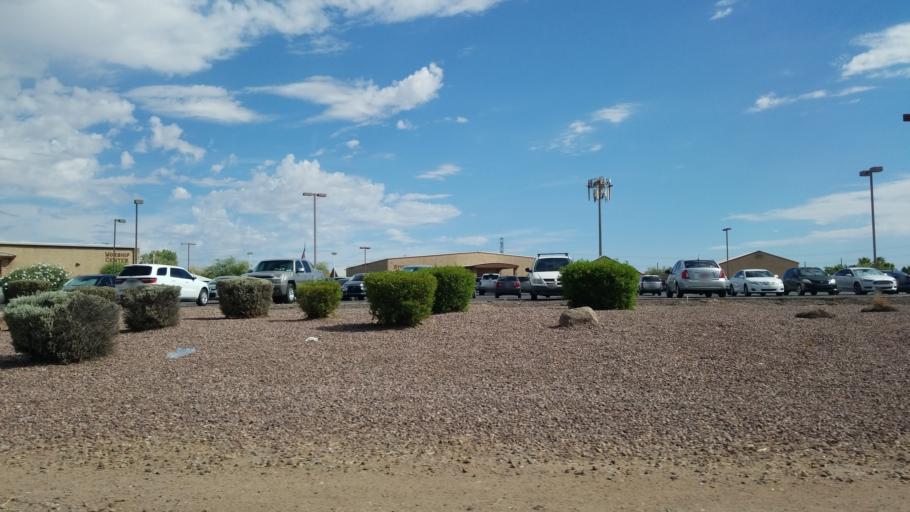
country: US
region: Arizona
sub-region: Maricopa County
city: Peoria
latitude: 33.5521
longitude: -112.2403
